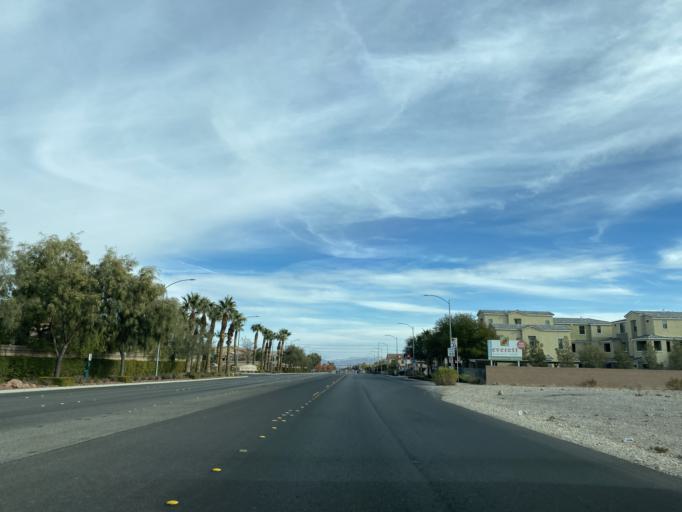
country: US
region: Nevada
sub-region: Clark County
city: Enterprise
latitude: 36.0411
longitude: -115.2508
